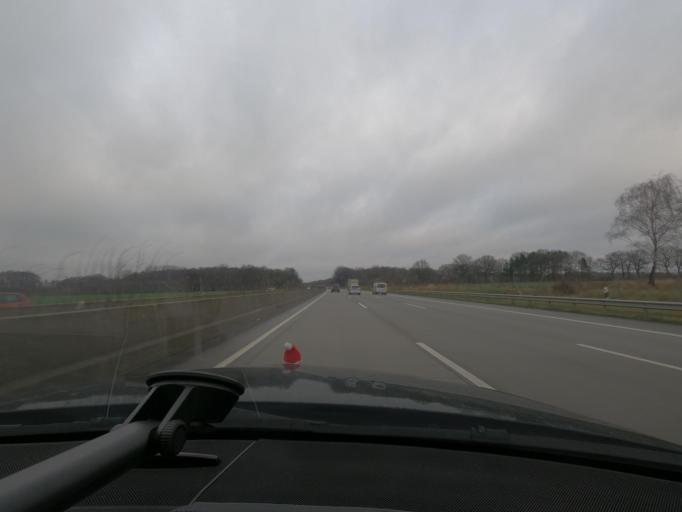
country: DE
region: Schleswig-Holstein
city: Bonningstedt
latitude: 53.6818
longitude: 9.9450
